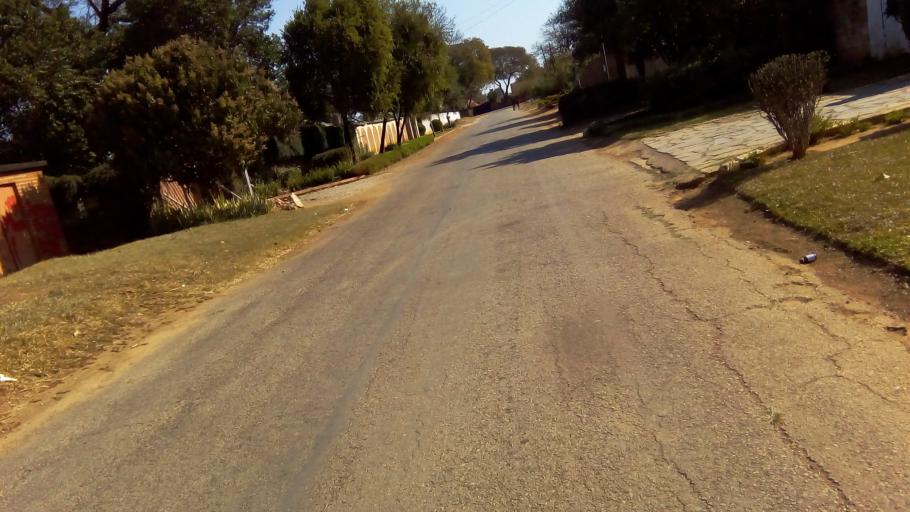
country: ZM
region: Lusaka
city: Lusaka
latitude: -15.4431
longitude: 28.3493
